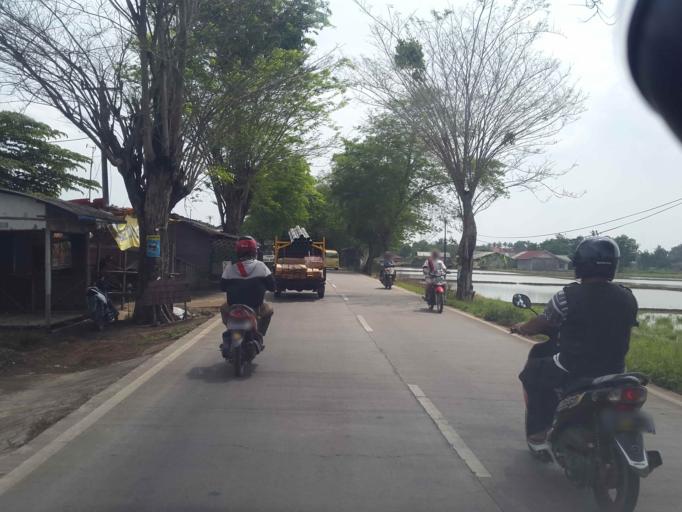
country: ID
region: West Java
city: Rengasdengklok
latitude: -6.2885
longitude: 107.3778
